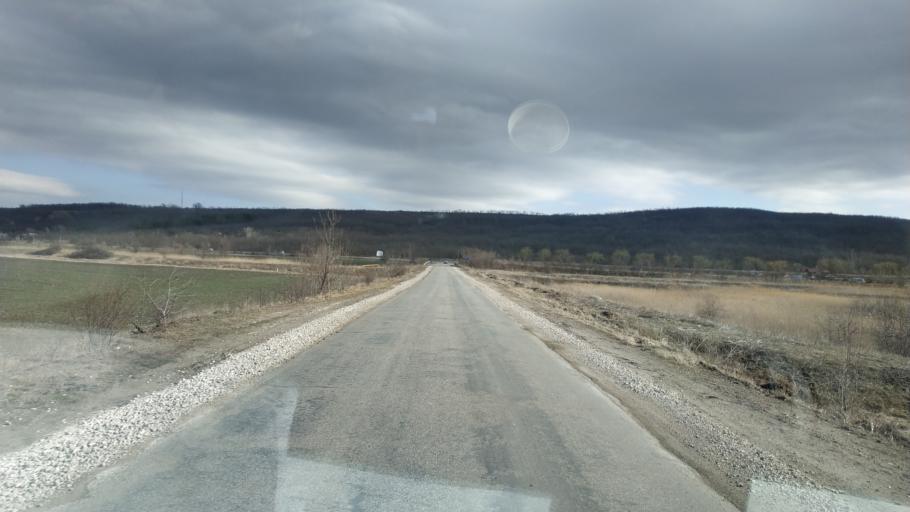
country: MD
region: Causeni
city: Causeni
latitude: 46.6376
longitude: 29.3713
